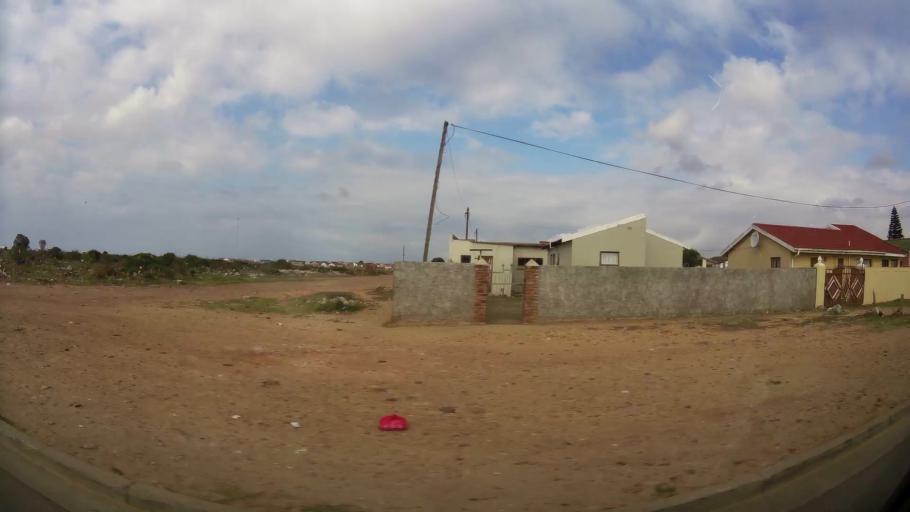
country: ZA
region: Eastern Cape
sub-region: Nelson Mandela Bay Metropolitan Municipality
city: Port Elizabeth
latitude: -33.8143
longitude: 25.5889
